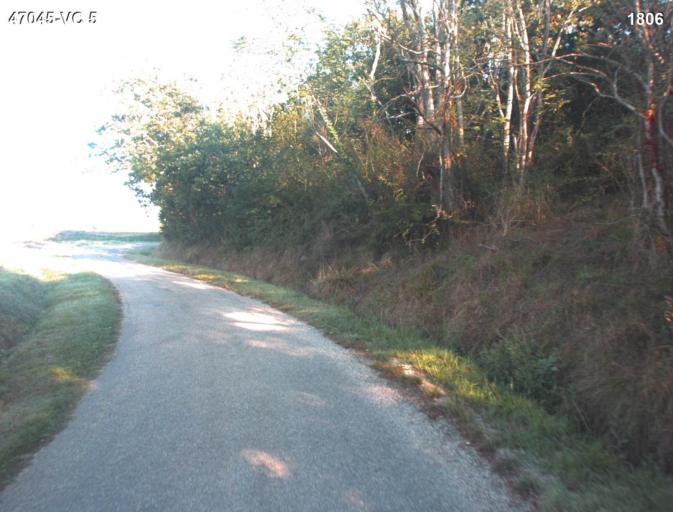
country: FR
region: Aquitaine
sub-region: Departement du Lot-et-Garonne
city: Nerac
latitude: 44.1450
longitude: 0.4060
